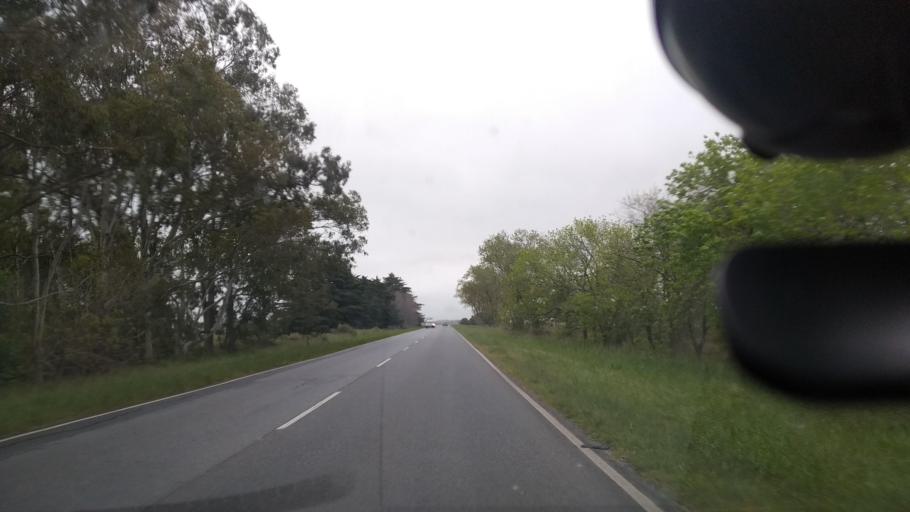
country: AR
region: Buenos Aires
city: Veronica
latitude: -35.3511
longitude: -57.4259
